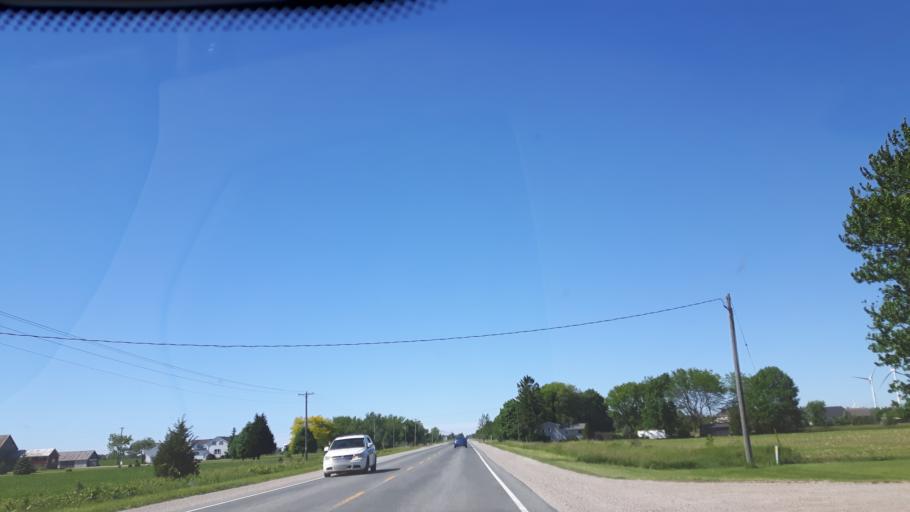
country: CA
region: Ontario
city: Bluewater
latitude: 43.4227
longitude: -81.7048
